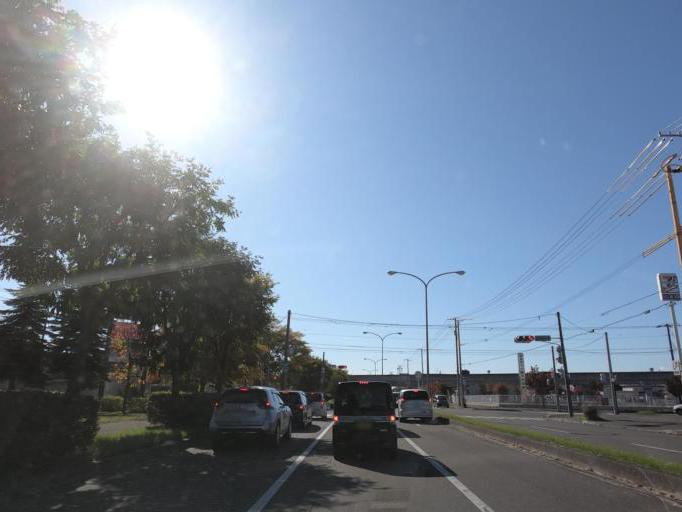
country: JP
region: Hokkaido
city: Obihiro
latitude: 42.9156
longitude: 143.2129
